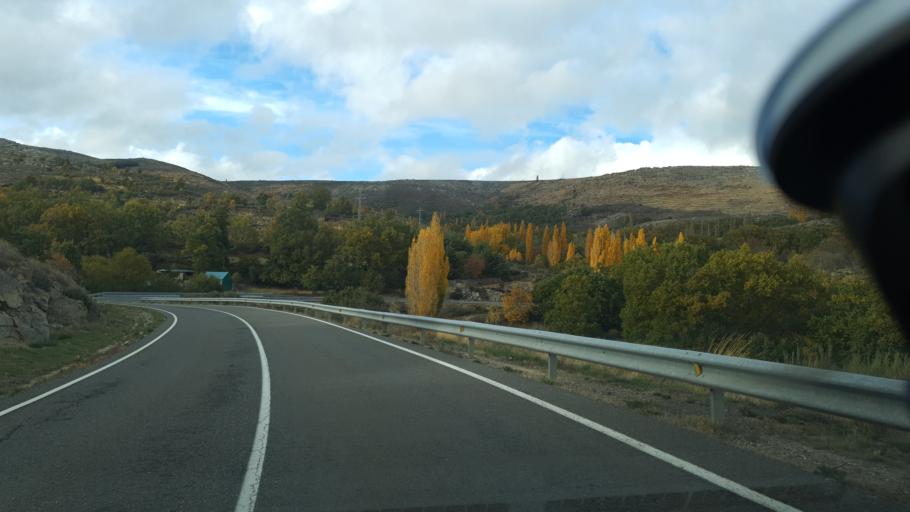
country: ES
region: Castille and Leon
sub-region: Provincia de Avila
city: Navalosa
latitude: 40.3973
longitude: -4.9406
